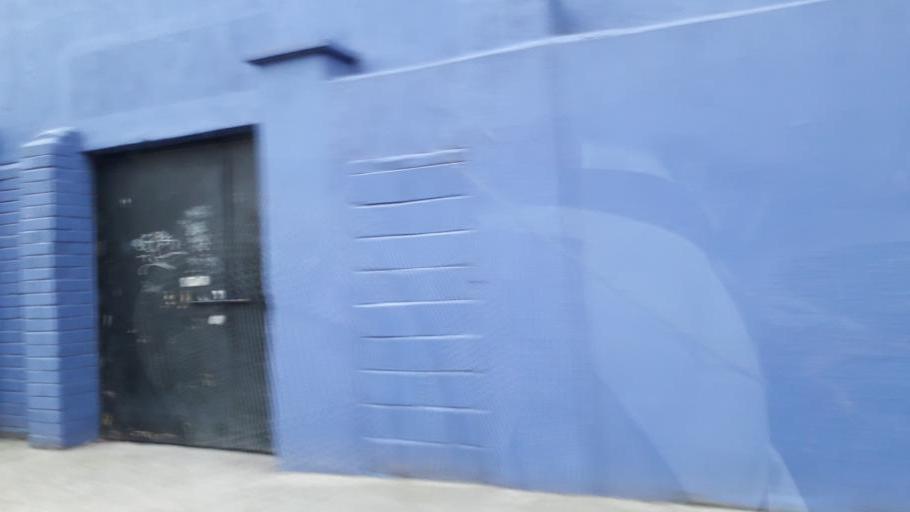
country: IE
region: Leinster
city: Rialto
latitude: 53.3401
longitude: -6.2830
